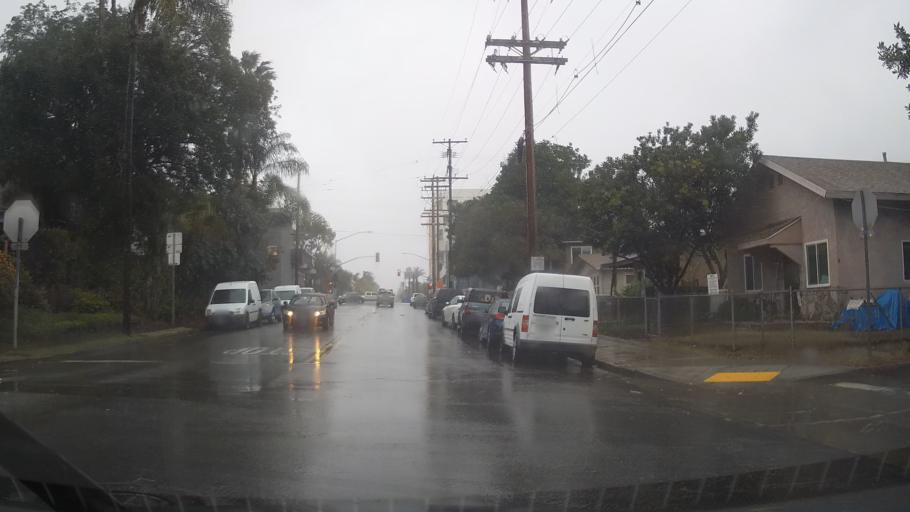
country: US
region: California
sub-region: San Diego County
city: San Diego
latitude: 32.7540
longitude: -117.1438
